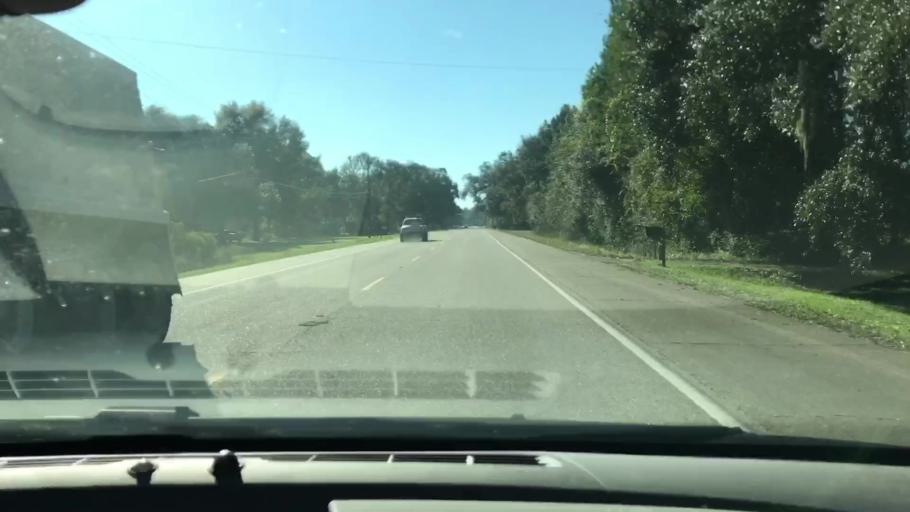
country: US
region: Louisiana
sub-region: Saint Tammany Parish
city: Pearl River
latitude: 30.4548
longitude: -89.8020
